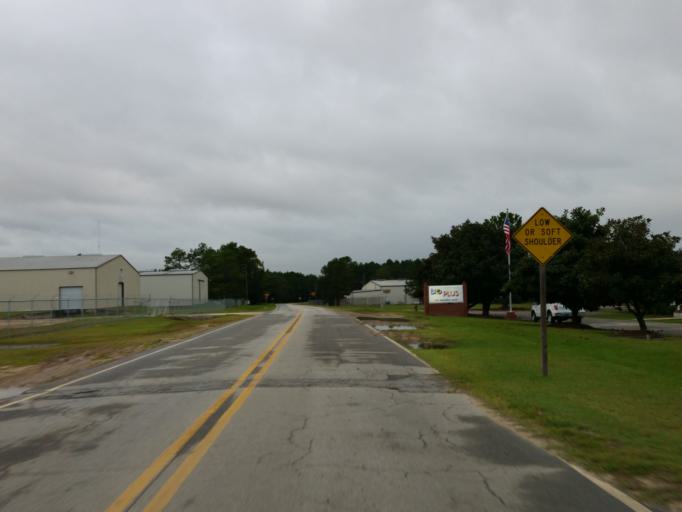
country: US
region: Georgia
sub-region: Turner County
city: Ashburn
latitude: 31.6825
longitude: -83.6386
